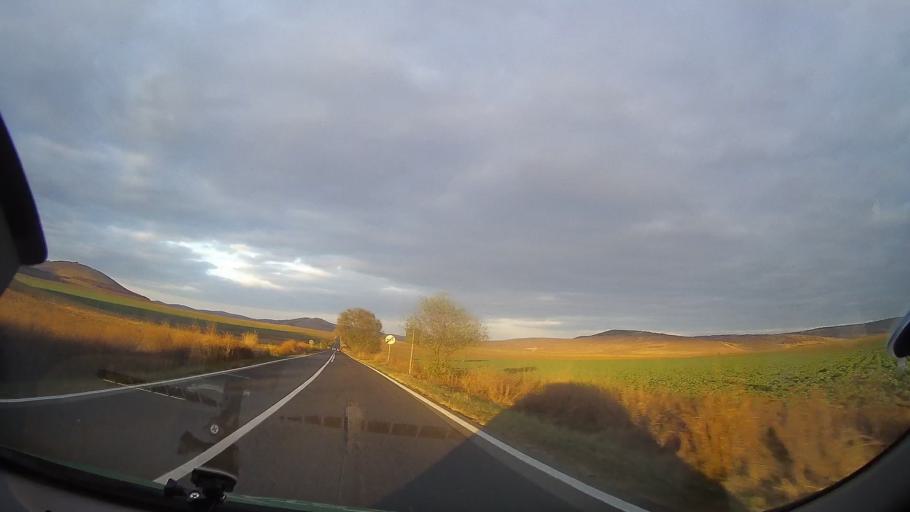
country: RO
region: Tulcea
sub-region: Comuna Nalbant
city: Nicolae Balcescu
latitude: 44.9695
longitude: 28.5381
